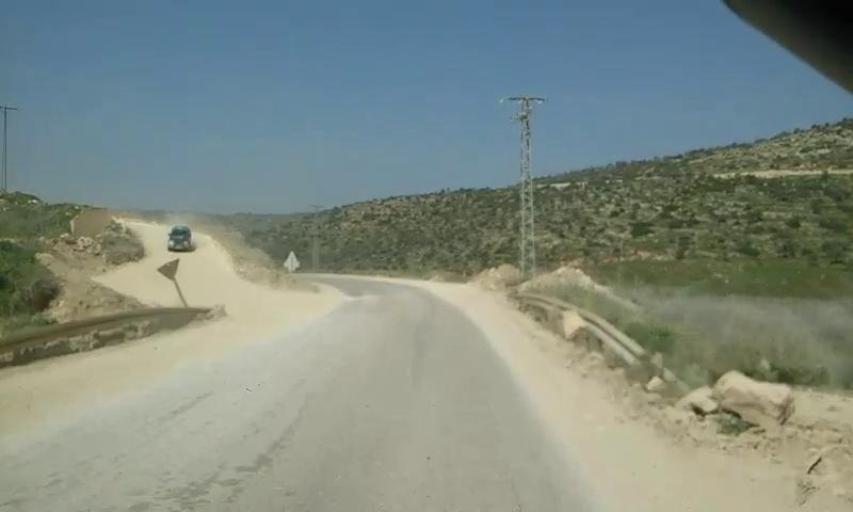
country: PS
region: West Bank
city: Az Zababidah
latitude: 32.4036
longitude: 35.3166
